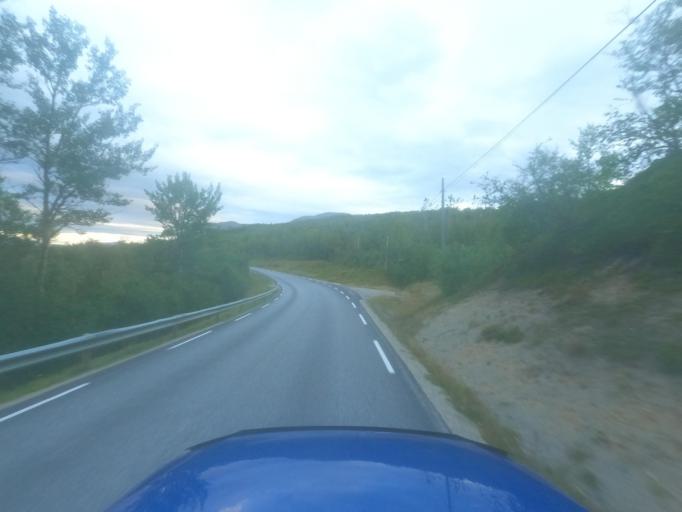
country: NO
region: Finnmark Fylke
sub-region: Porsanger
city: Lakselv
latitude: 70.1560
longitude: 24.8905
